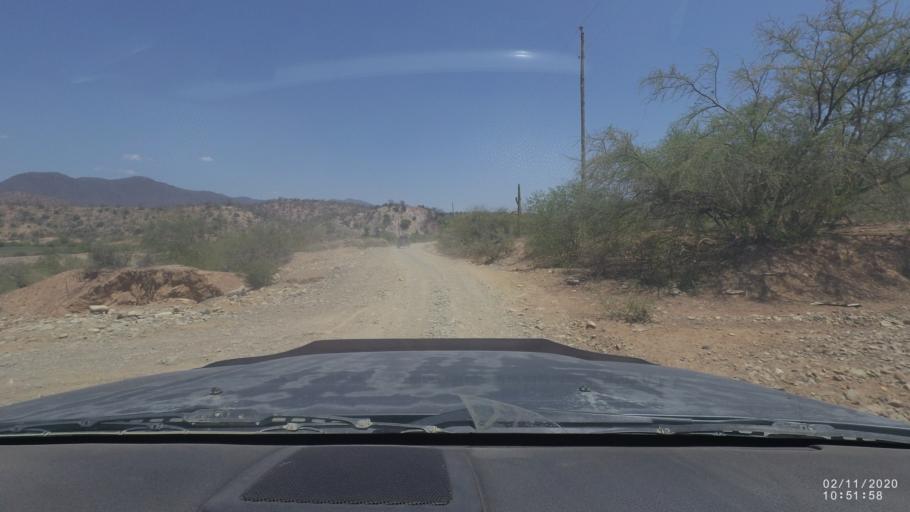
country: BO
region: Cochabamba
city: Aiquile
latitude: -18.1871
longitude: -64.8675
